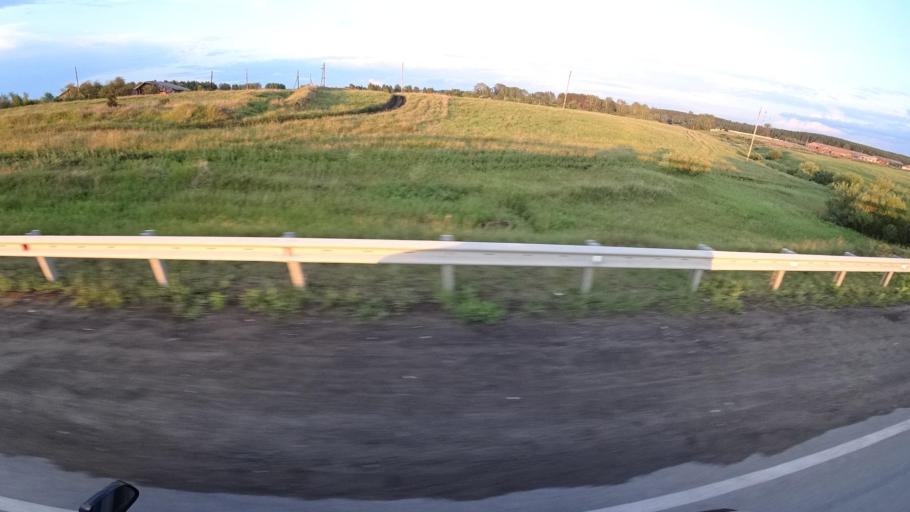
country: RU
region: Sverdlovsk
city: Kamyshlov
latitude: 56.8739
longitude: 62.7117
